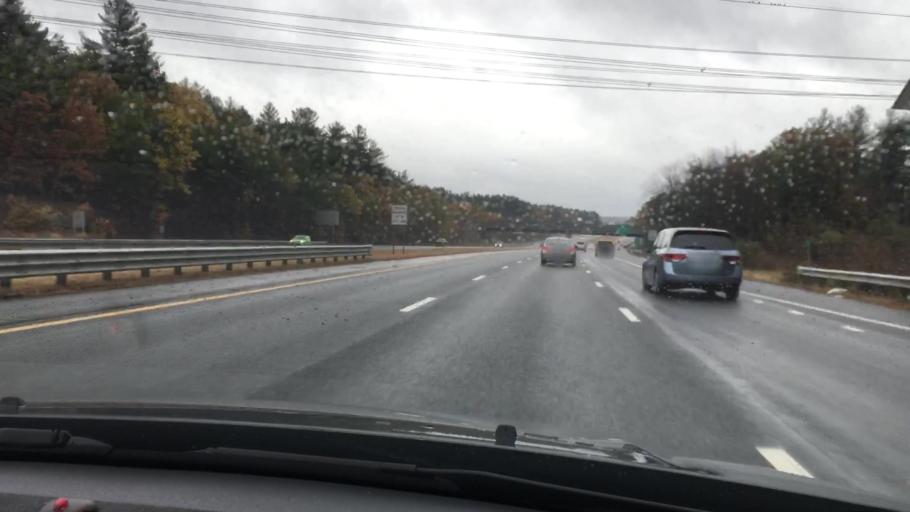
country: US
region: Massachusetts
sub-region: Middlesex County
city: Tyngsboro
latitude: 42.6888
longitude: -71.4436
